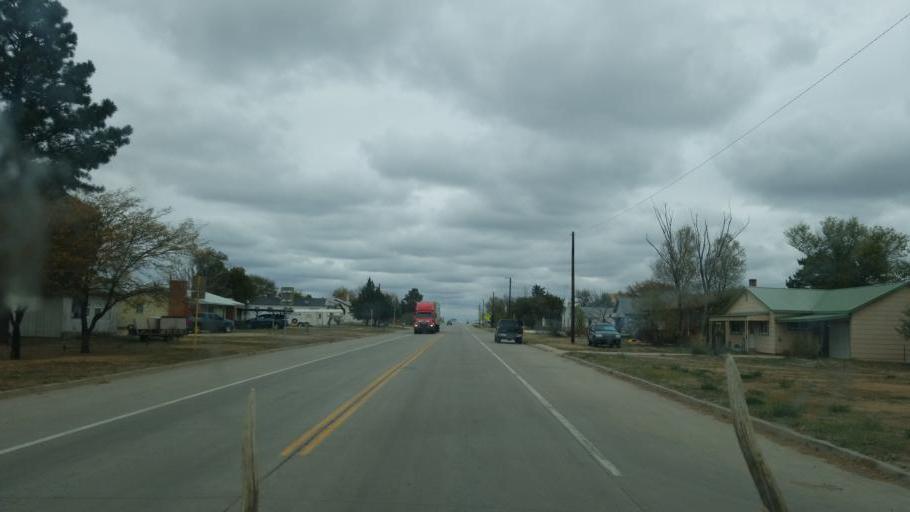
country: US
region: Colorado
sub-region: Kiowa County
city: Eads
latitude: 38.4809
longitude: -102.7858
